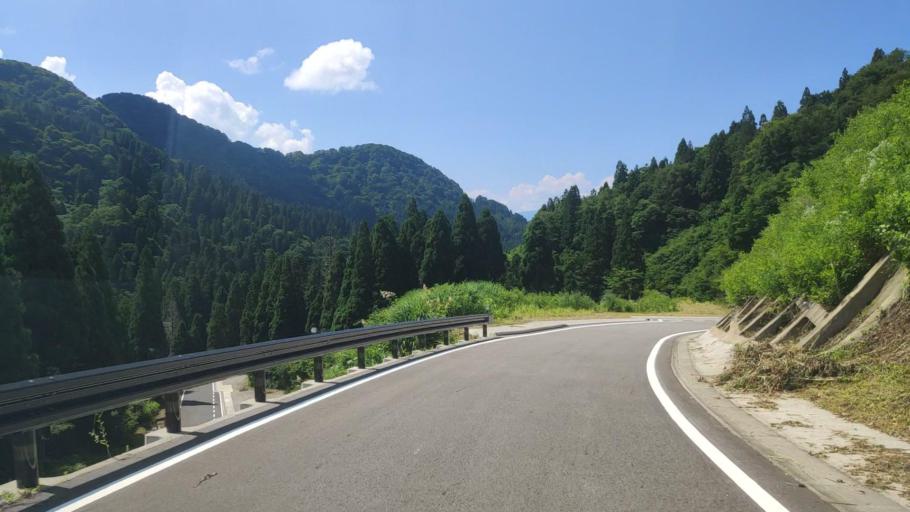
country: JP
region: Fukui
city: Katsuyama
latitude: 36.1445
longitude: 136.5202
